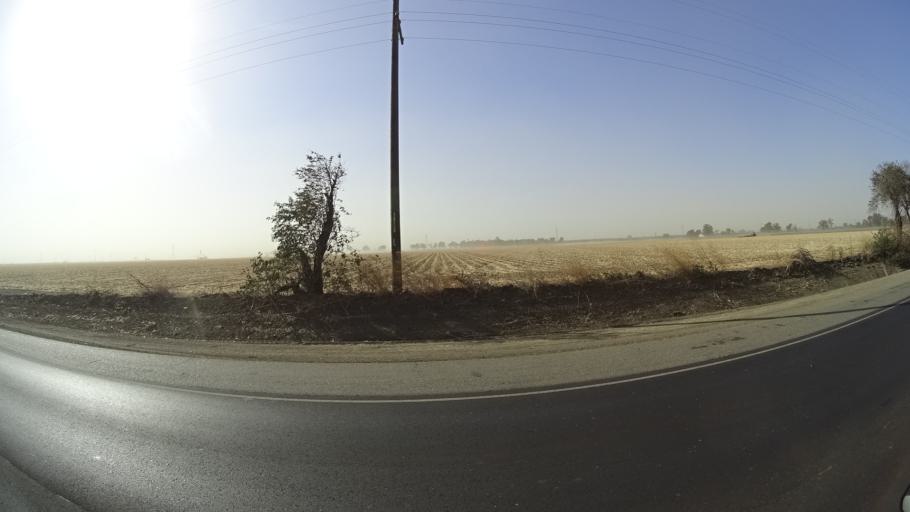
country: US
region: California
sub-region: Yolo County
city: Woodland
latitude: 38.7828
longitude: -121.7284
